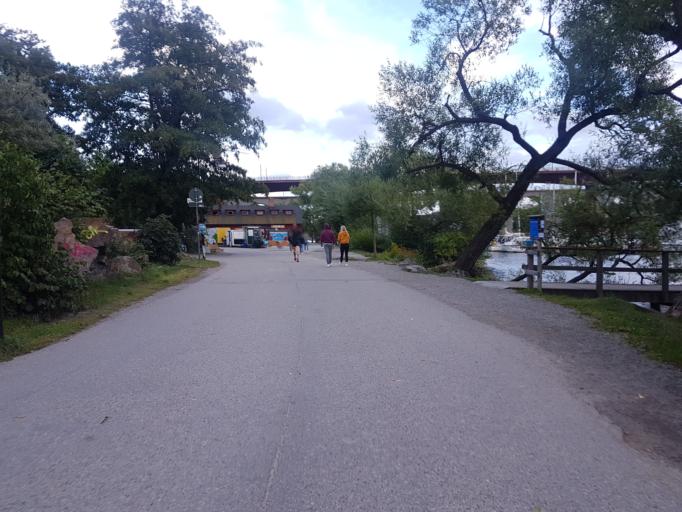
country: SE
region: Stockholm
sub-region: Stockholms Kommun
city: Arsta
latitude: 59.3112
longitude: 18.0404
